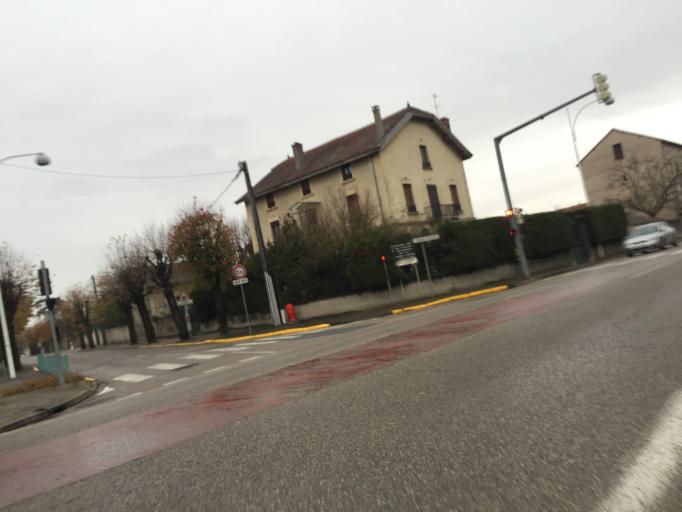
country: FR
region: Rhone-Alpes
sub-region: Departement de l'Ain
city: Saint-Maurice-de-Beynost
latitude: 45.8291
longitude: 4.9767
